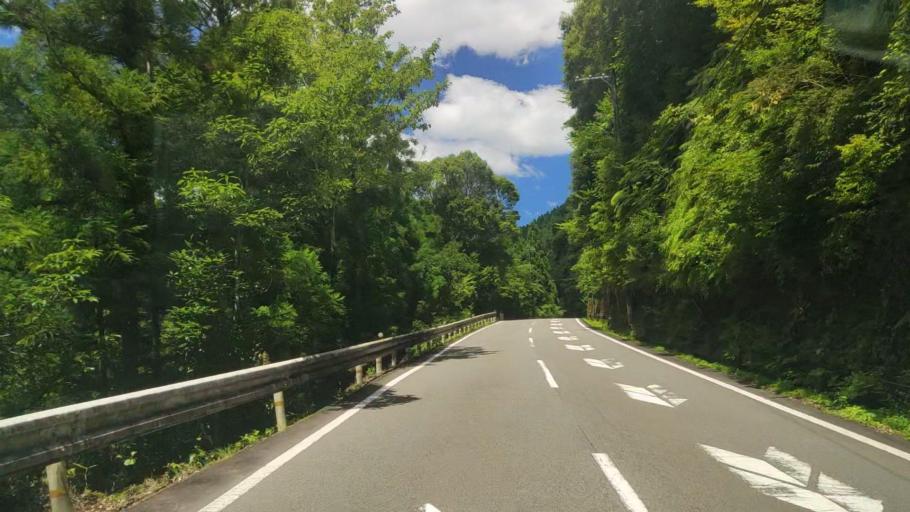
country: JP
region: Mie
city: Owase
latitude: 33.9961
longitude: 136.0130
